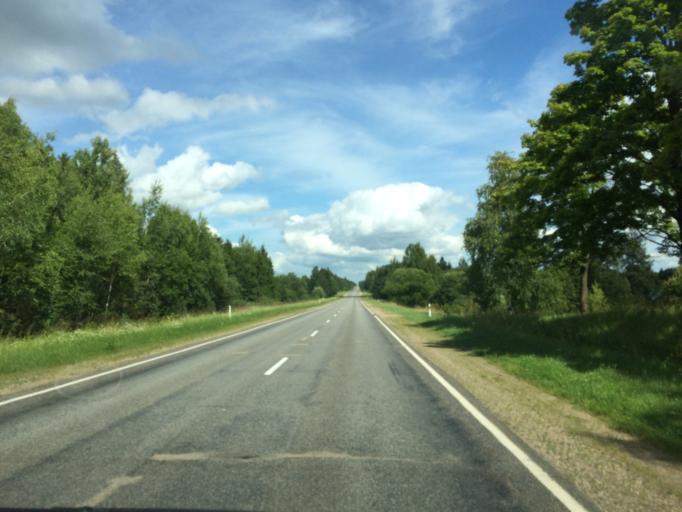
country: LV
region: Rezekne
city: Rezekne
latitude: 56.6377
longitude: 27.4767
